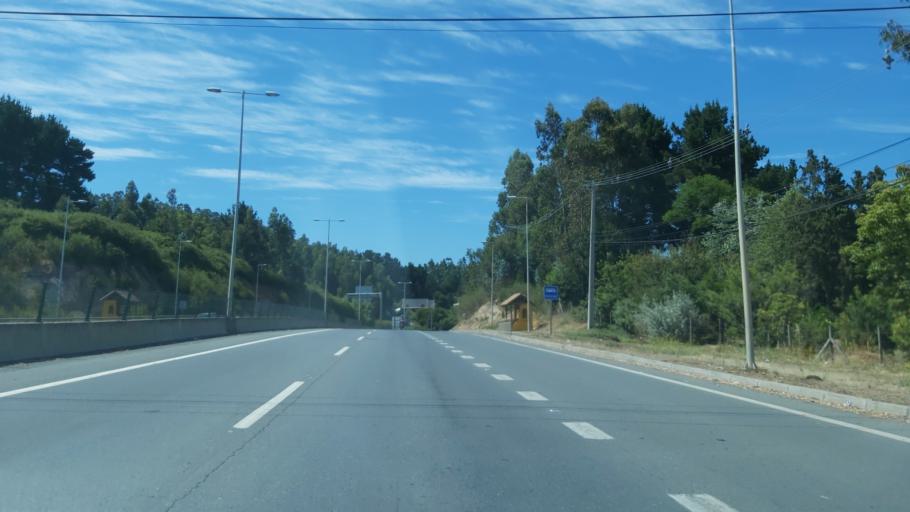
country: CL
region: Biobio
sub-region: Provincia de Concepcion
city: Coronel
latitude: -37.0494
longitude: -73.1416
